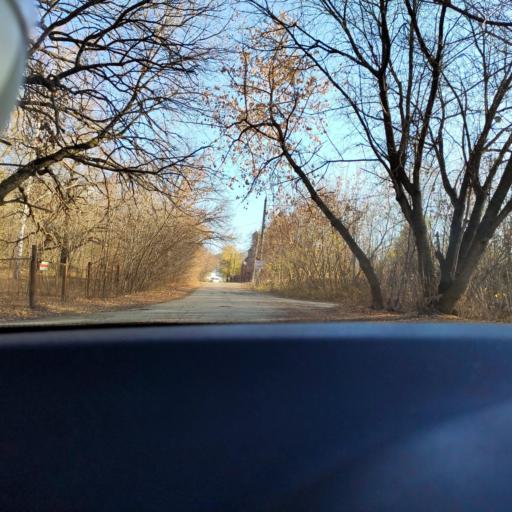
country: RU
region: Samara
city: Samara
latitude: 53.2240
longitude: 50.1636
